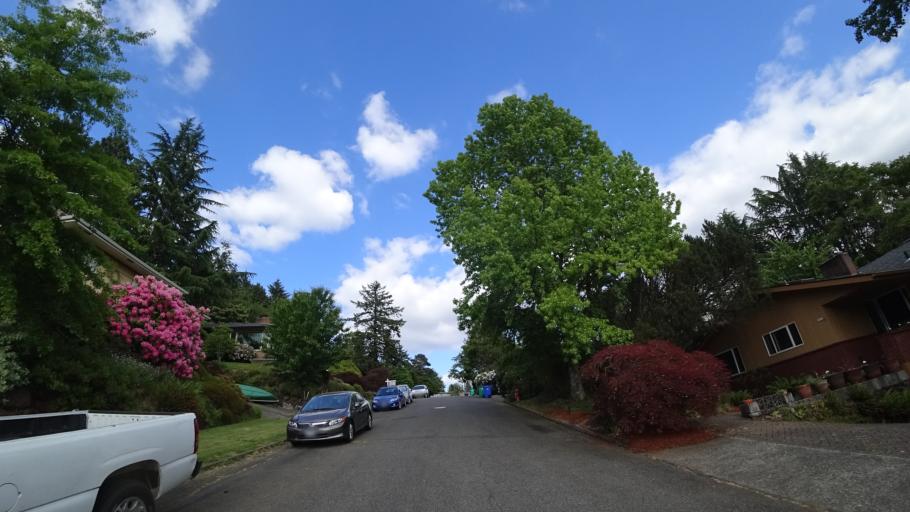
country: US
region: Oregon
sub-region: Washington County
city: Garden Home-Whitford
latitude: 45.4771
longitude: -122.7181
